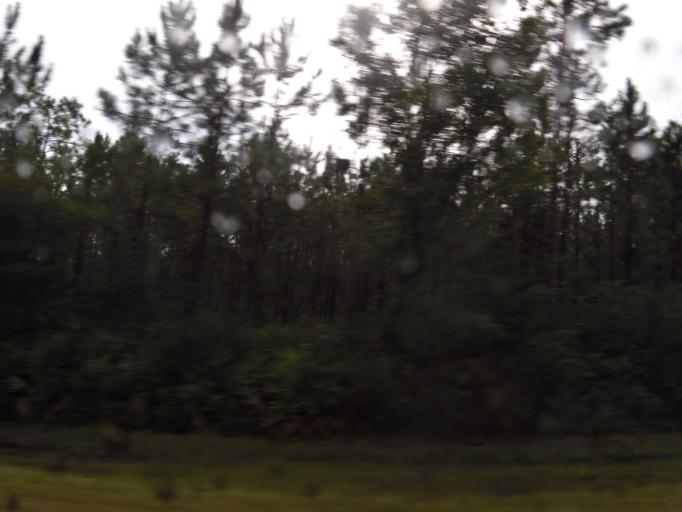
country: US
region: Florida
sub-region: Duval County
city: Baldwin
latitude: 30.4851
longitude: -82.0420
